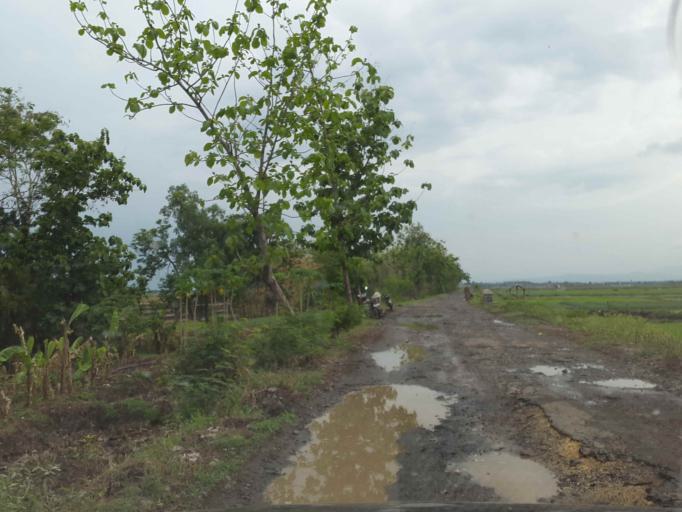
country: ID
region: Central Java
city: Ketanggungan
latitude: -6.9484
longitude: 108.9452
